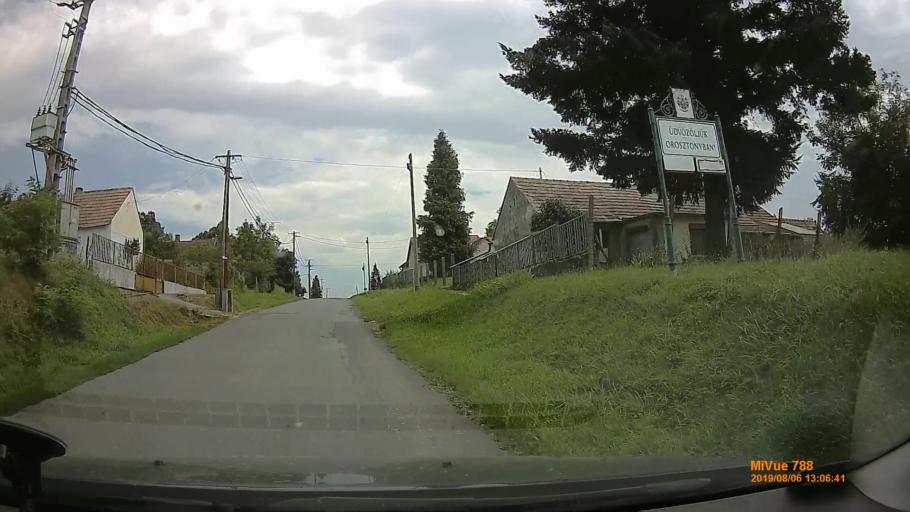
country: HU
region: Zala
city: Pacsa
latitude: 46.6299
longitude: 17.0550
